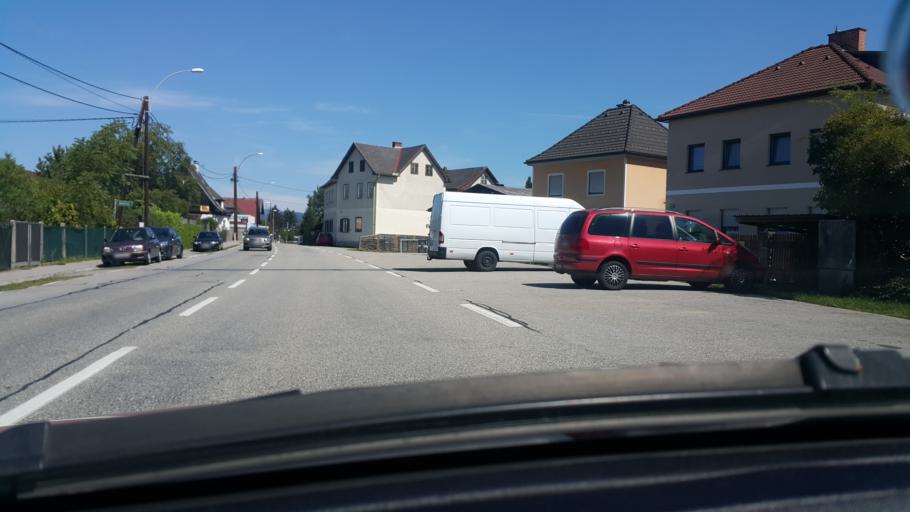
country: AT
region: Styria
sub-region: Graz Stadt
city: Wetzelsdorf
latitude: 47.0463
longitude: 15.4178
